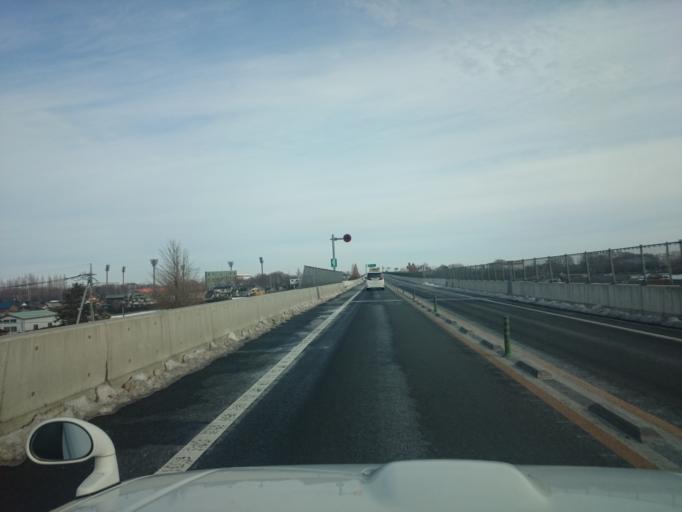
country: JP
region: Saitama
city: Satte
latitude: 36.0772
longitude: 139.7541
